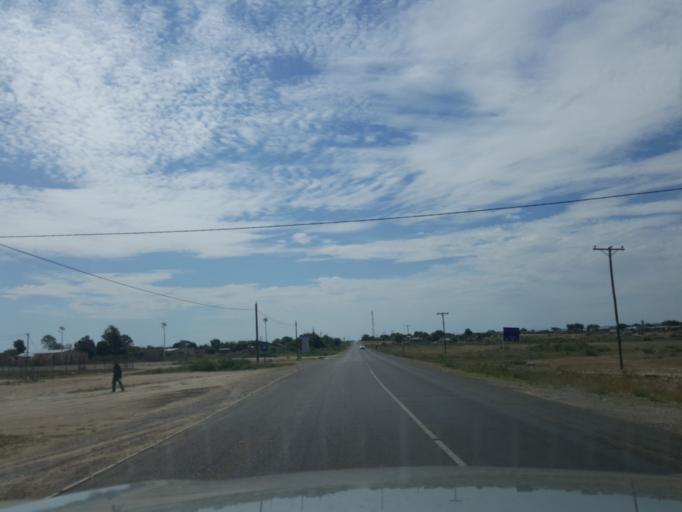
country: BW
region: Kweneng
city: Letlhakeng
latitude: -24.1121
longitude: 25.0356
